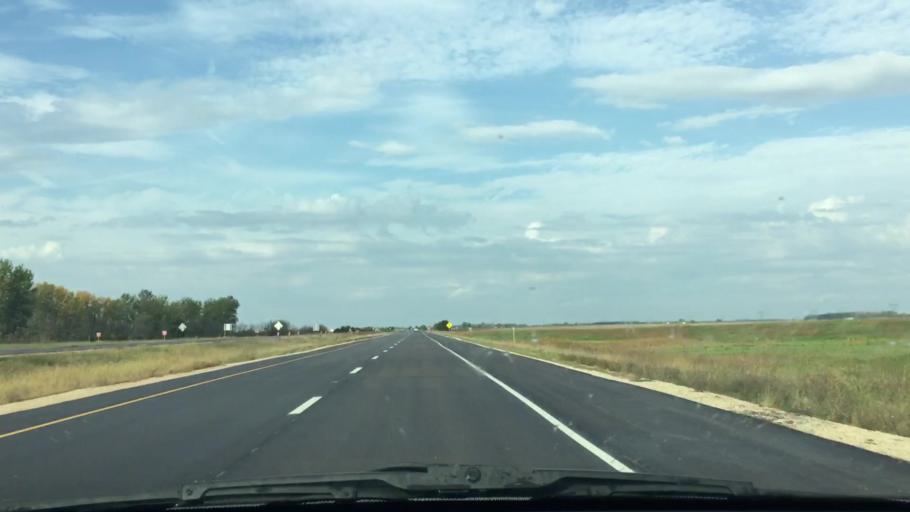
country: US
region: Illinois
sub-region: Whiteside County
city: Erie
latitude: 41.6891
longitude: -90.0981
